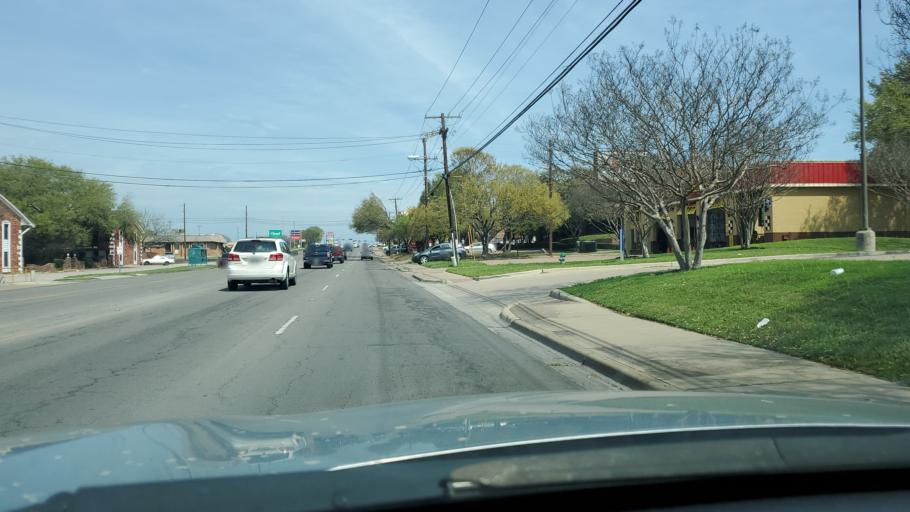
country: US
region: Texas
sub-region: Bell County
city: Temple
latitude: 31.0654
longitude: -97.3709
